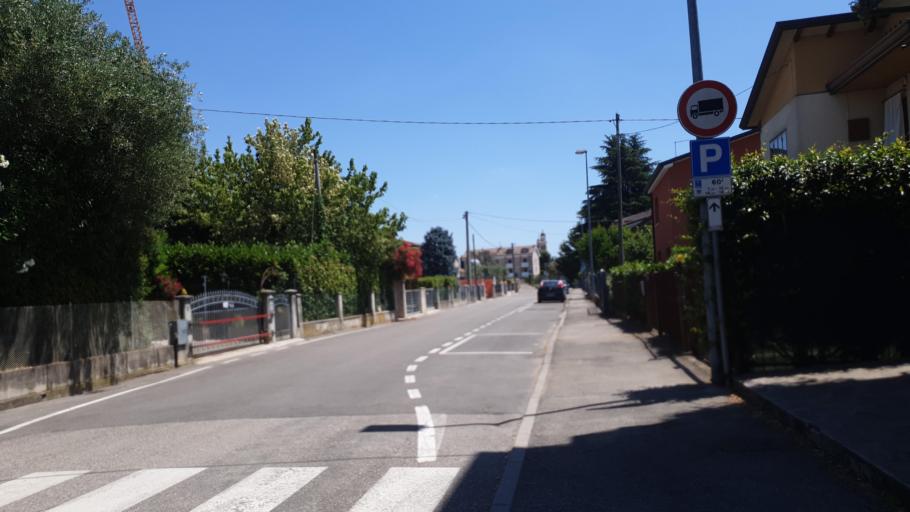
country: IT
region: Veneto
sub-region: Provincia di Padova
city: Camposampiero
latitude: 45.5666
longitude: 11.9249
